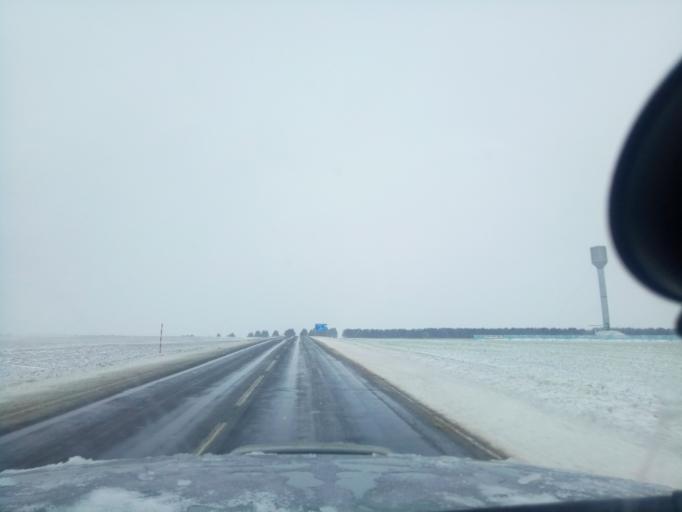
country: BY
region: Minsk
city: Haradzyeya
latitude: 53.2986
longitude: 26.5753
